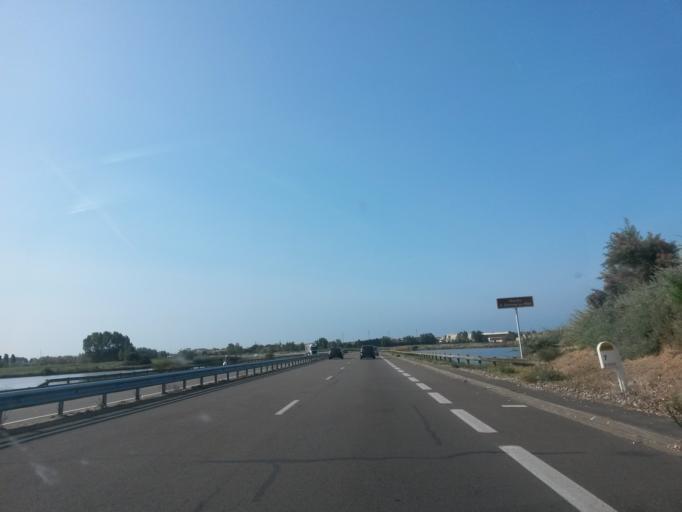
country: FR
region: Pays de la Loire
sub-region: Departement de la Vendee
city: Les Sables-d'Olonne
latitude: 46.5119
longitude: -1.7928
